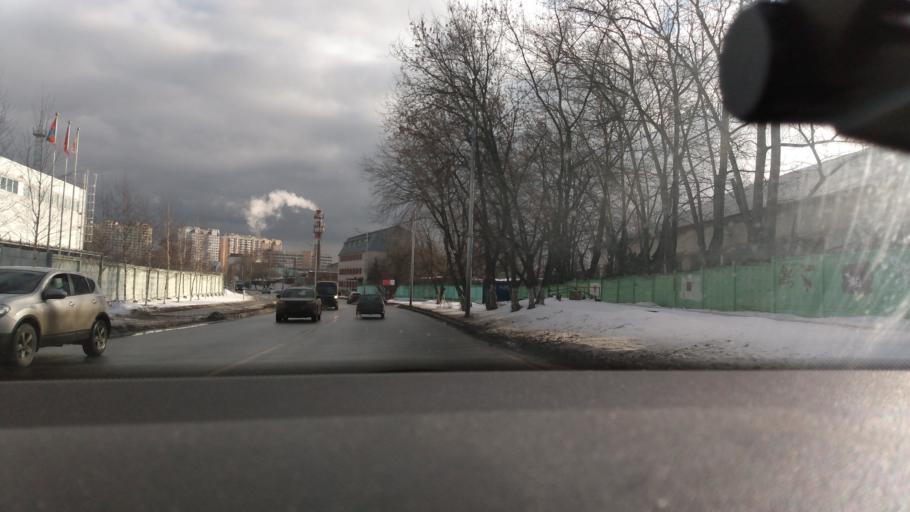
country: RU
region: Moskovskaya
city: Balashikha
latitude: 55.8332
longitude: 37.9461
